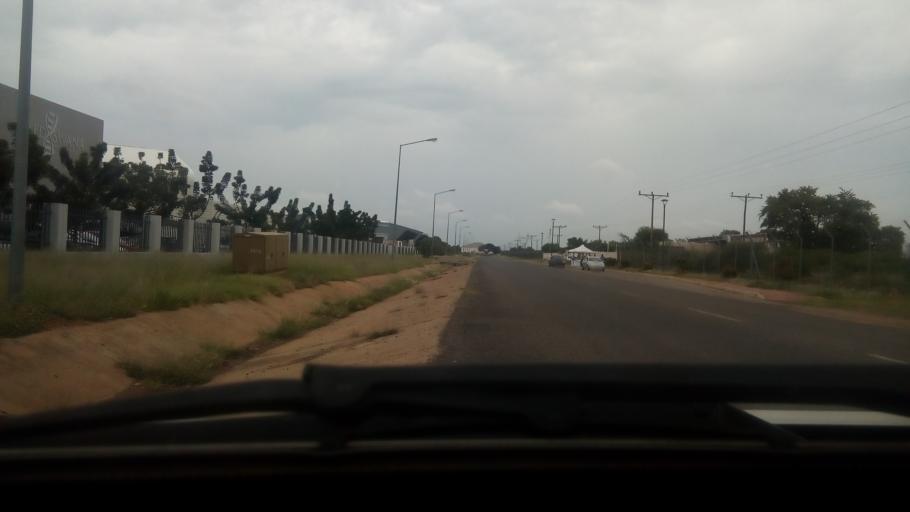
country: BW
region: Kweneng
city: Mmopone
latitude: -24.5885
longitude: 25.9113
